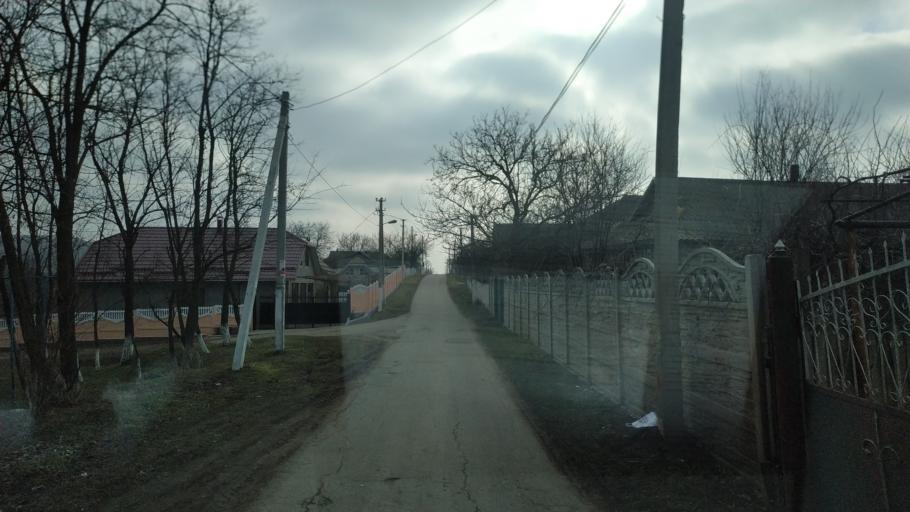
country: MD
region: Hincesti
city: Dancu
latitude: 46.8831
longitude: 28.3206
